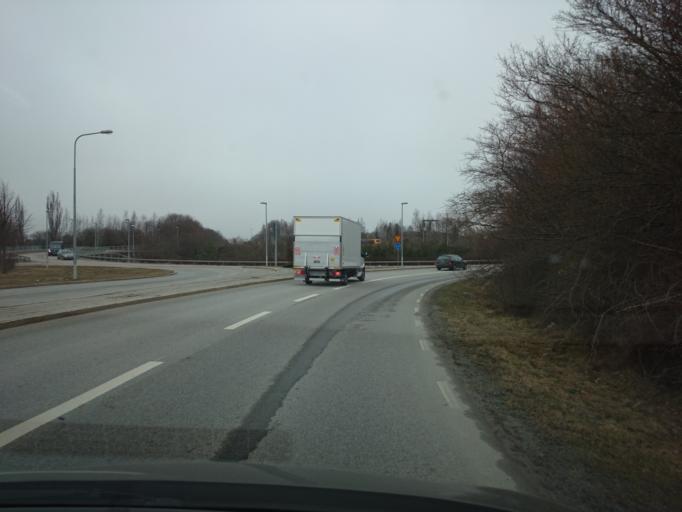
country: SE
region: Uppsala
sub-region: Uppsala Kommun
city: Gamla Uppsala
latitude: 59.8795
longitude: 17.6225
